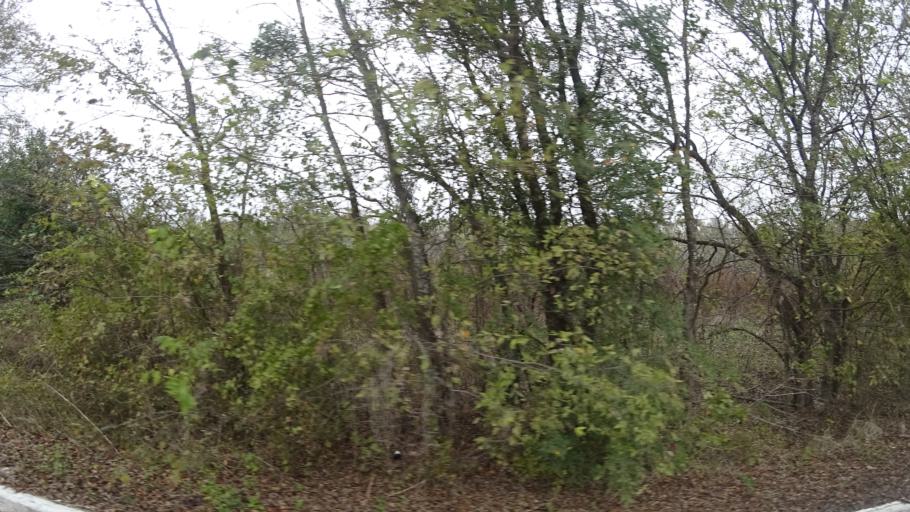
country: US
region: Texas
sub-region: Travis County
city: Pflugerville
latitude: 30.3798
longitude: -97.6337
